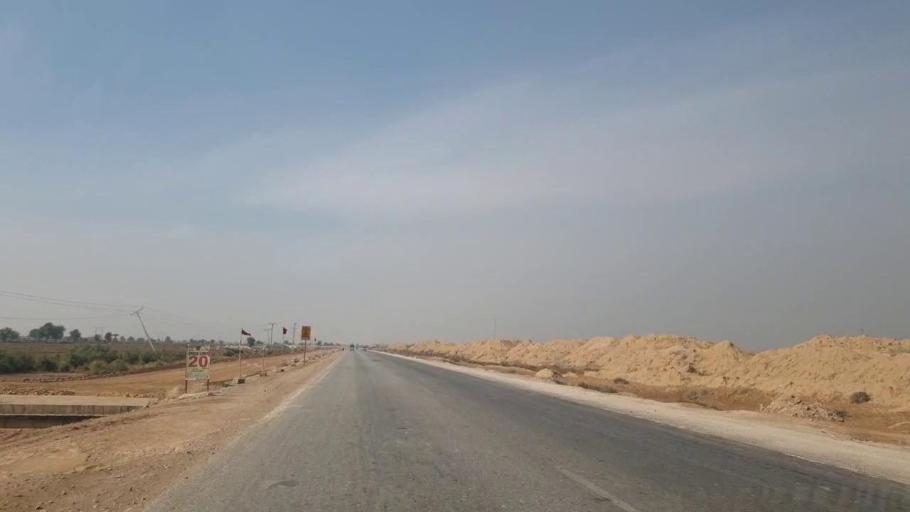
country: PK
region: Sindh
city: Sann
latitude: 26.0063
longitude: 68.1546
